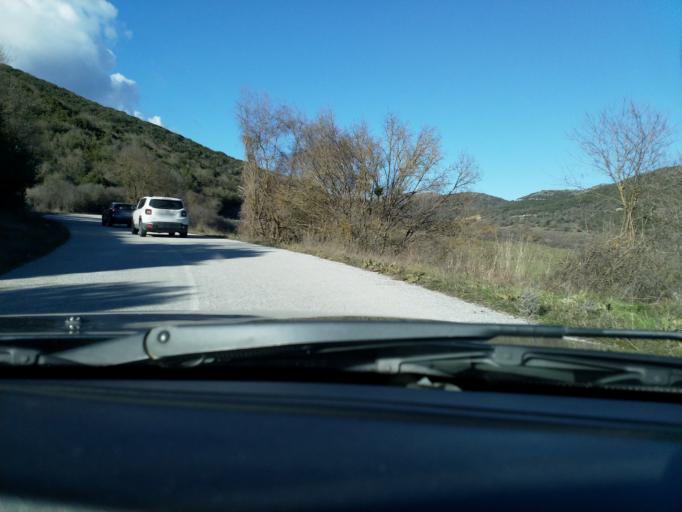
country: GR
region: Epirus
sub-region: Nomos Ioanninon
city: Kalpaki
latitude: 39.8882
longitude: 20.6730
